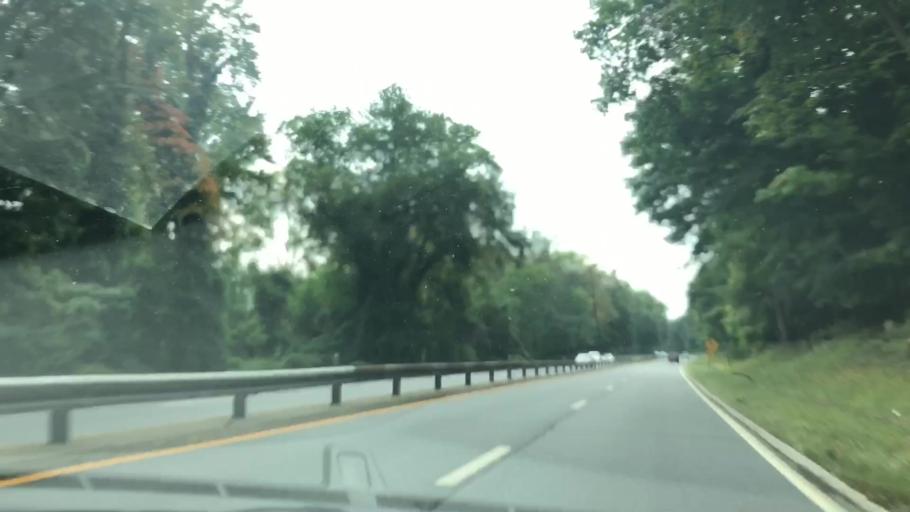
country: US
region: New York
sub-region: Westchester County
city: Hastings-on-Hudson
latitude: 40.9976
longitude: -73.8593
